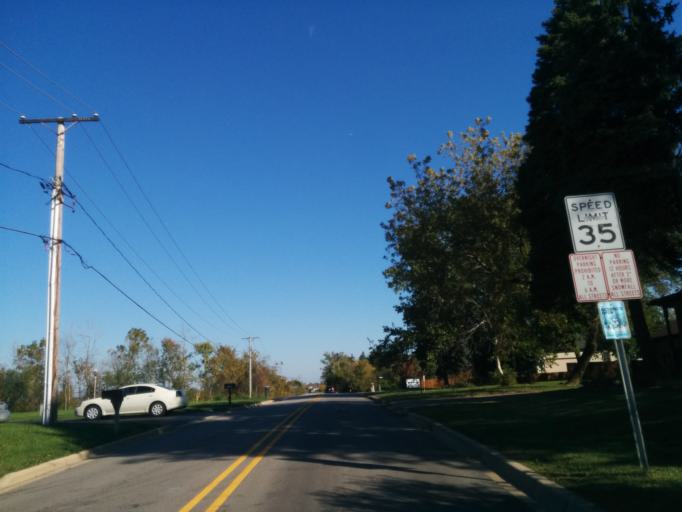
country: US
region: Illinois
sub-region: Cook County
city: Bartlett
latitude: 41.9442
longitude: -88.1771
